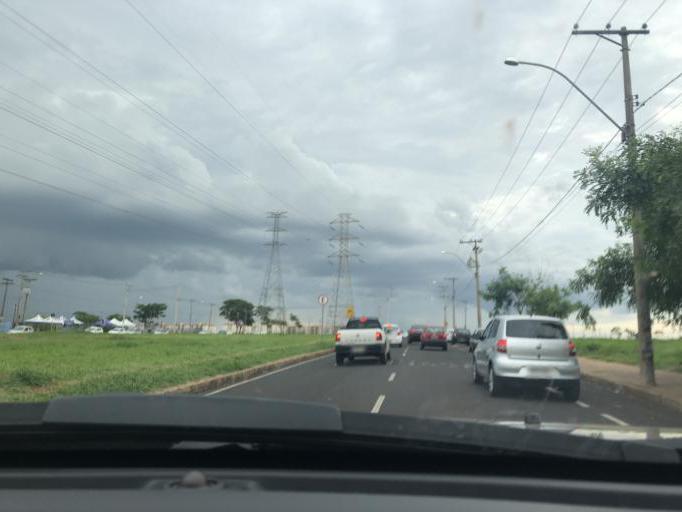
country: BR
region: Sao Paulo
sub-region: Sao Jose Do Rio Preto
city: Sao Jose do Rio Preto
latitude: -20.8421
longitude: -49.4129
